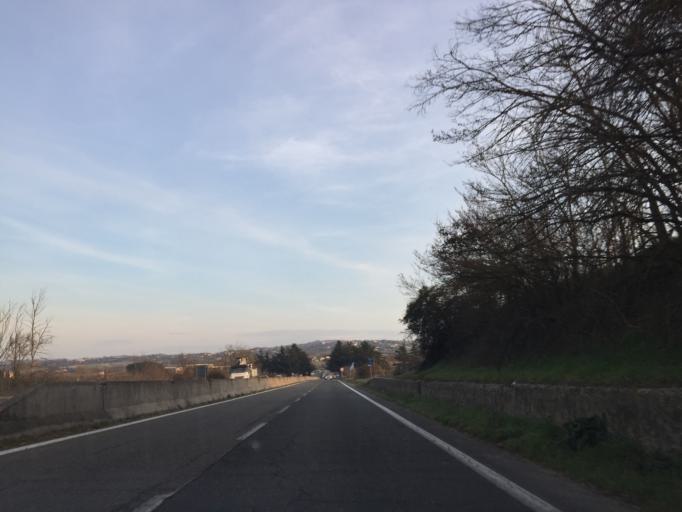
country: IT
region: Latium
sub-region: Citta metropolitana di Roma Capitale
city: Campagnano di Roma
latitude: 42.1571
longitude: 12.3419
